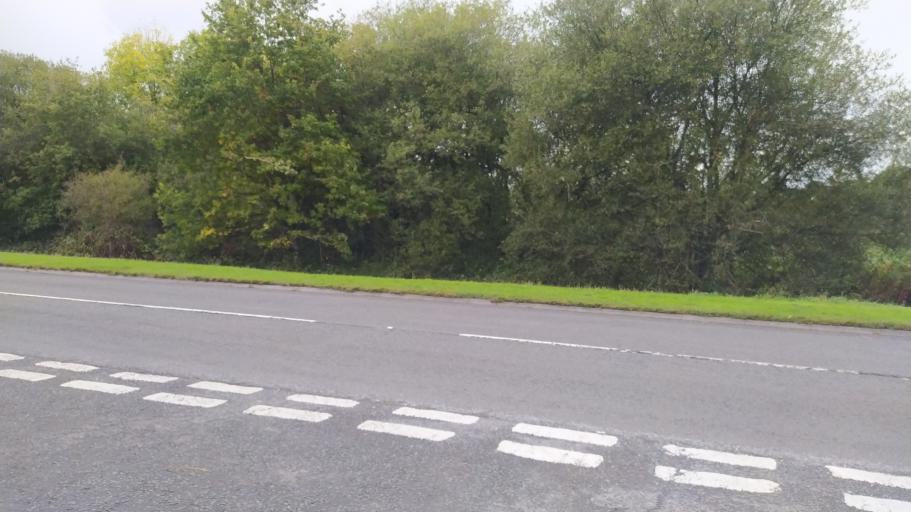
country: GB
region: England
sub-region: Dorset
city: Shaftesbury
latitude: 51.0459
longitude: -2.1837
